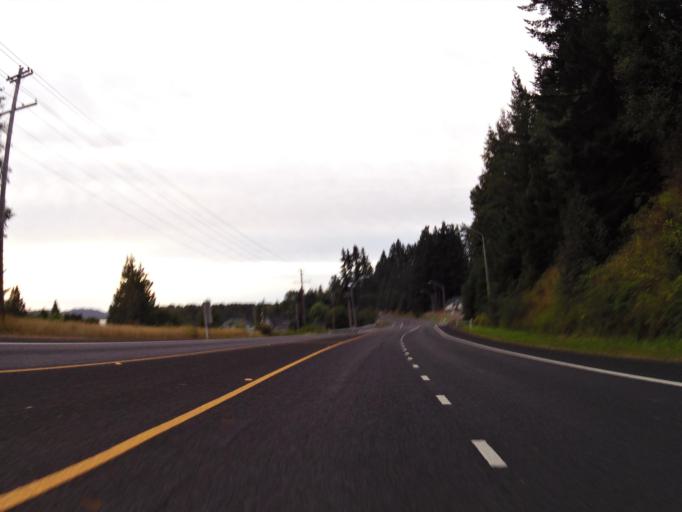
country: US
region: Washington
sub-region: Wahkiakum County
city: Cathlamet
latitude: 46.2038
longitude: -123.3811
